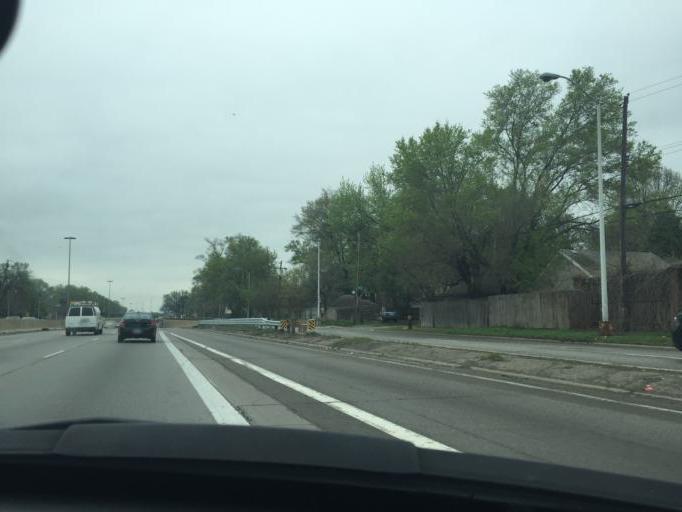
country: US
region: Michigan
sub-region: Oakland County
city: Oak Park
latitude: 42.3967
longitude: -83.2183
